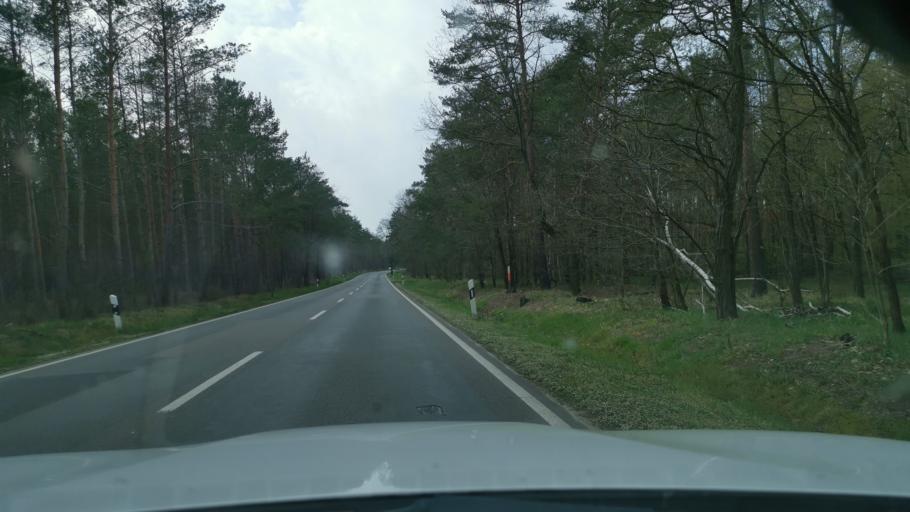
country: DE
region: Saxony
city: Bad Duben
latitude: 51.5649
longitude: 12.5321
